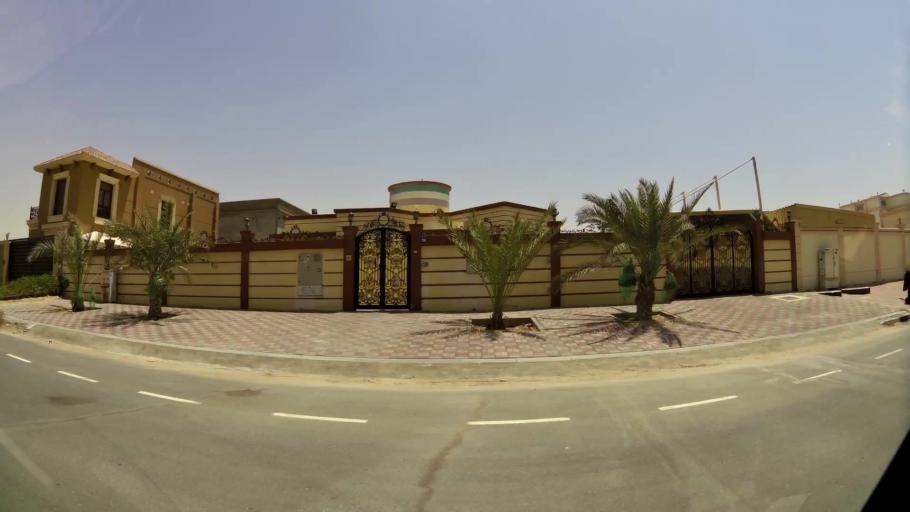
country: AE
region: Dubai
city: Dubai
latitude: 25.0889
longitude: 55.2095
